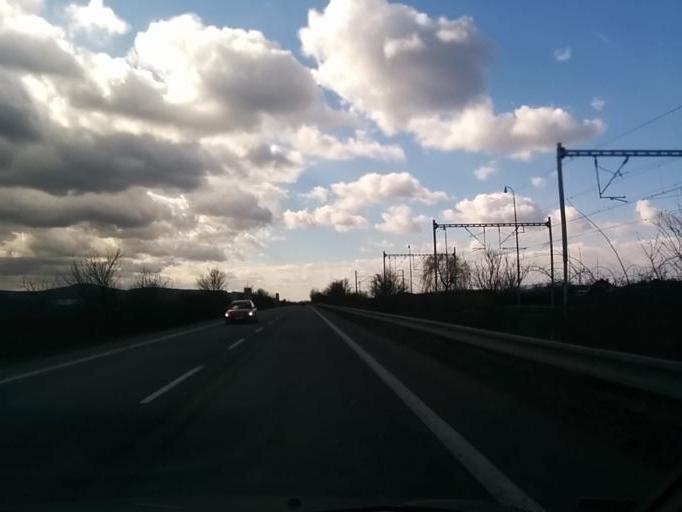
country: SK
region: Trenciansky
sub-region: Okres Trencin
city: Trencin
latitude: 48.8561
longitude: 17.9467
